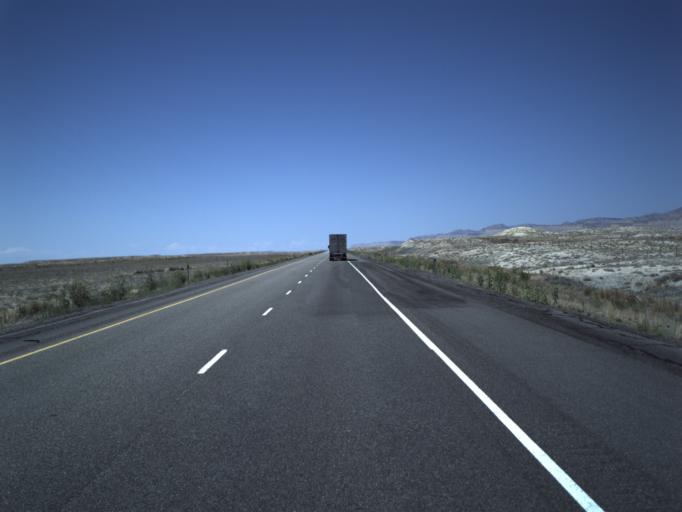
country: US
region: Utah
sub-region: Grand County
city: Moab
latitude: 38.9365
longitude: -109.4676
